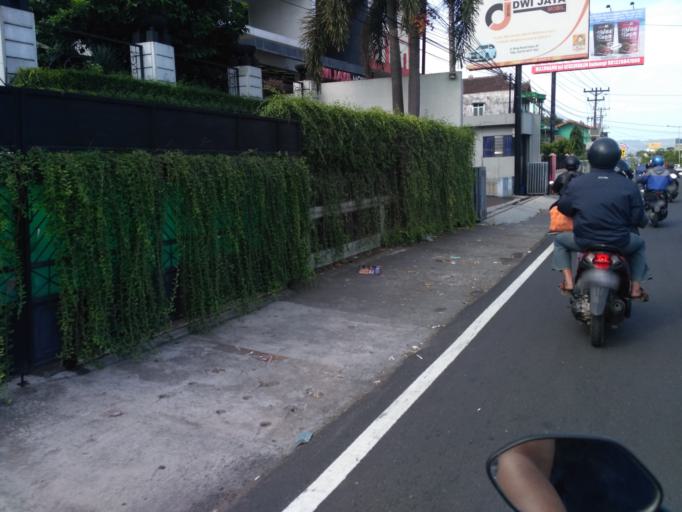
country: ID
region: Daerah Istimewa Yogyakarta
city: Depok
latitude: -7.7617
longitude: 110.4124
